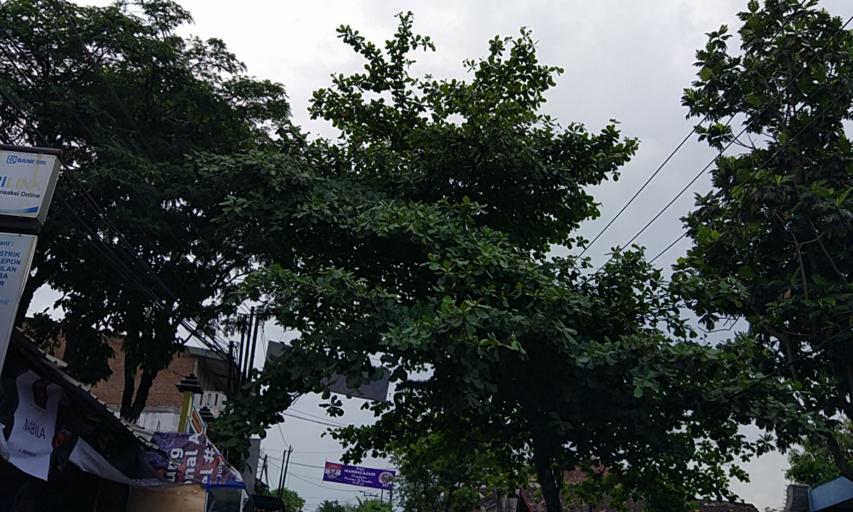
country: ID
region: West Java
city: Bandung
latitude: -6.8997
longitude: 107.6811
